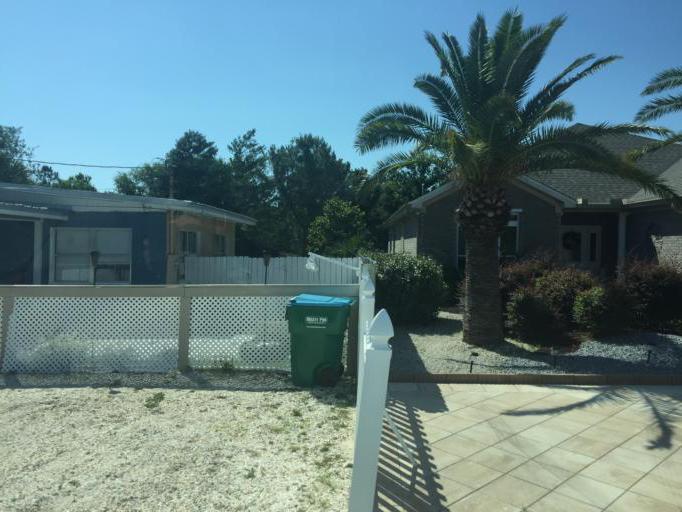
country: US
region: Florida
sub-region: Bay County
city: Panama City Beach
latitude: 30.2017
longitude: -85.8466
